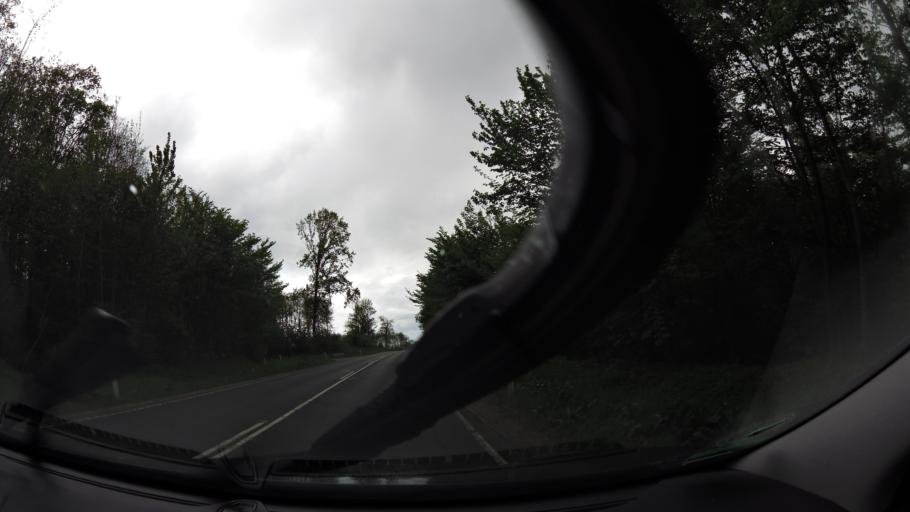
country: DK
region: South Denmark
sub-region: Nyborg Kommune
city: Nyborg
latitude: 55.2724
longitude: 10.7661
